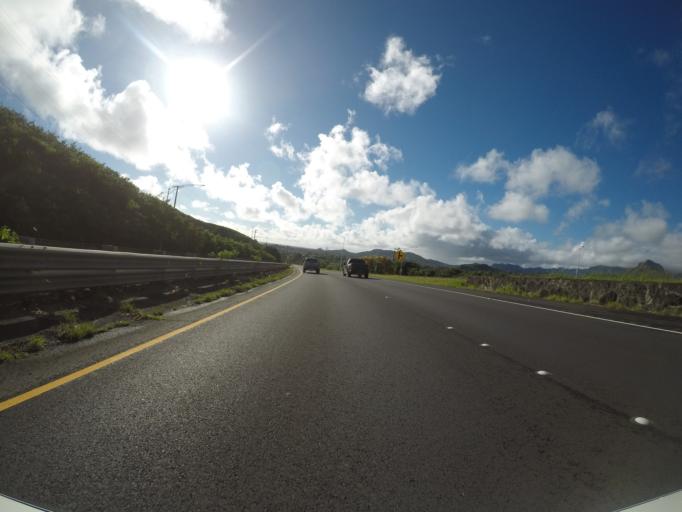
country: US
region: Hawaii
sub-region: Honolulu County
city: Kailua
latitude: 21.4064
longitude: -157.7656
